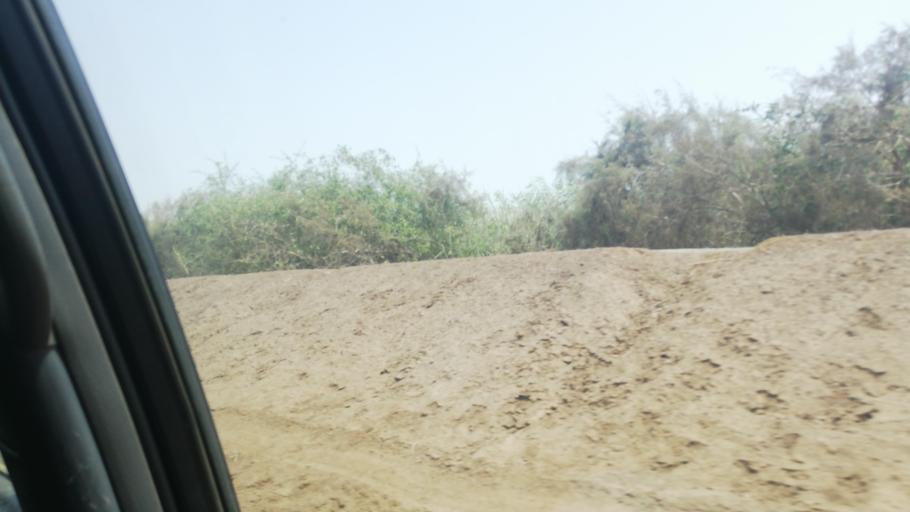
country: SN
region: Saint-Louis
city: Saint-Louis
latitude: 16.4068
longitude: -16.2976
